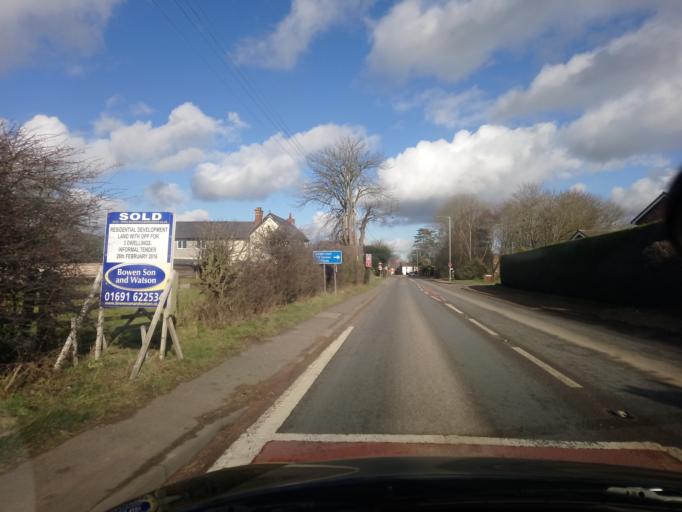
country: GB
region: England
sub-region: Shropshire
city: Astley
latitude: 52.7721
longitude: -2.7113
